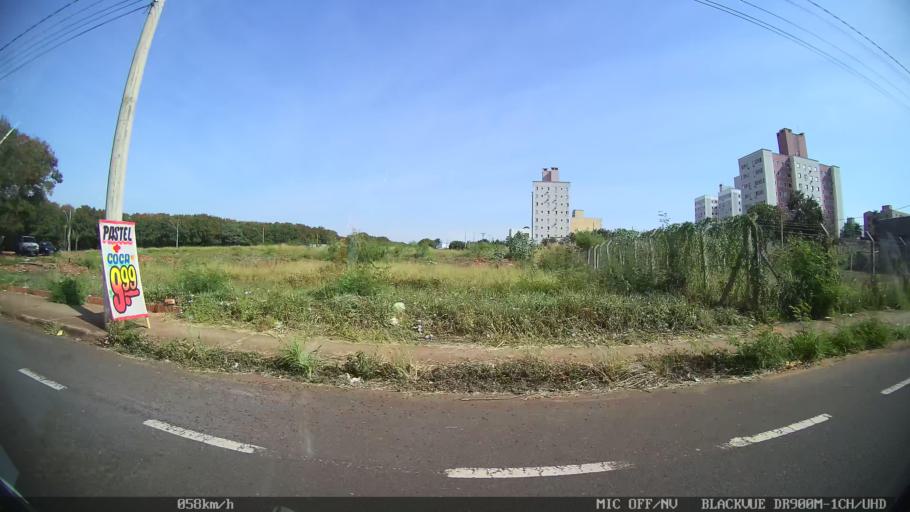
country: BR
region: Sao Paulo
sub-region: Sao Jose Do Rio Preto
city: Sao Jose do Rio Preto
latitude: -20.7966
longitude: -49.4018
